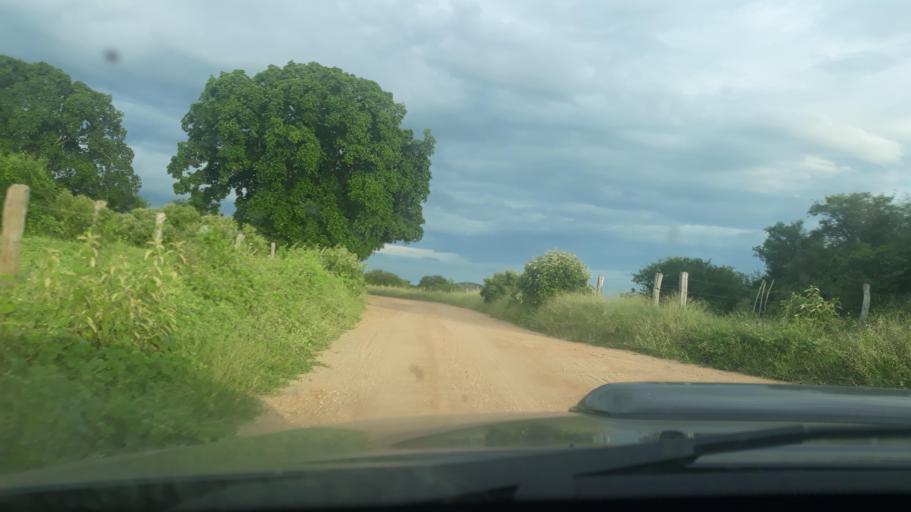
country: BR
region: Bahia
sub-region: Riacho De Santana
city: Riacho de Santana
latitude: -13.9062
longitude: -42.9726
